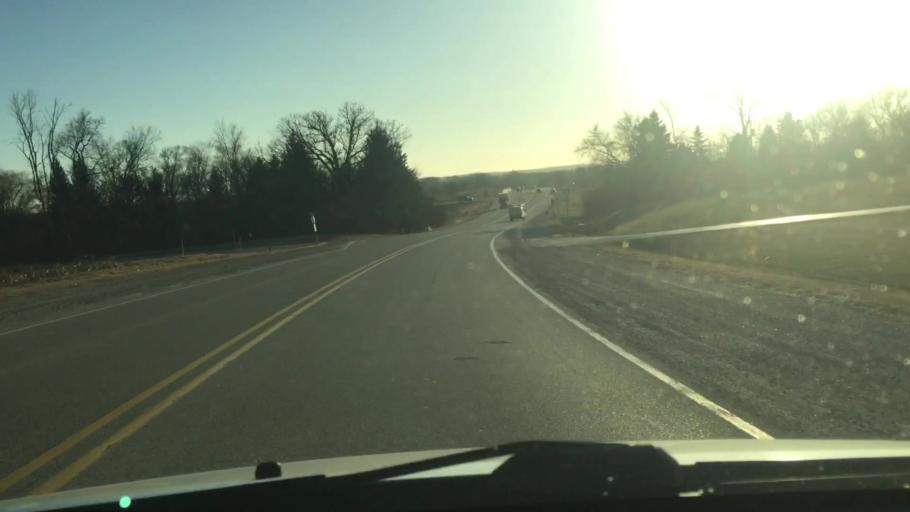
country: US
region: Wisconsin
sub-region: Waukesha County
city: Pewaukee
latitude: 43.0984
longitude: -88.2695
